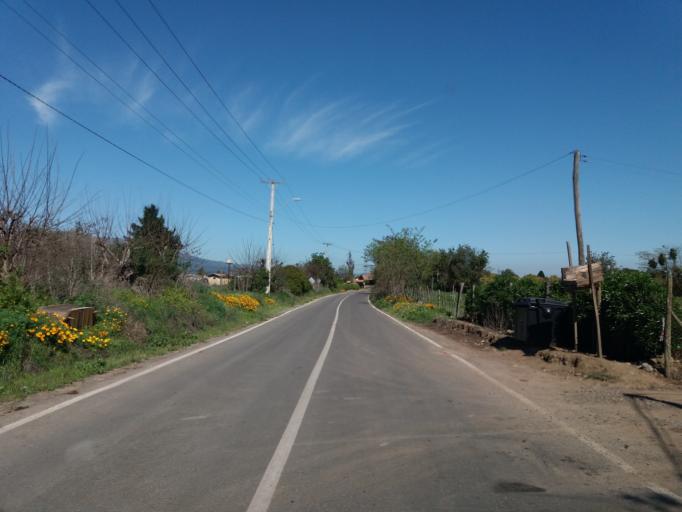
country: CL
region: Valparaiso
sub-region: Provincia de Marga Marga
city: Limache
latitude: -33.0012
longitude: -71.1836
